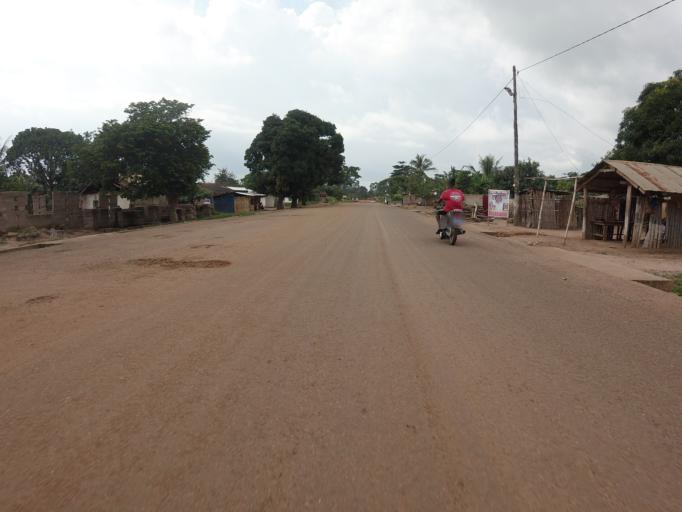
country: GH
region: Volta
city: Kpandu
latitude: 6.9581
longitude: 0.4588
